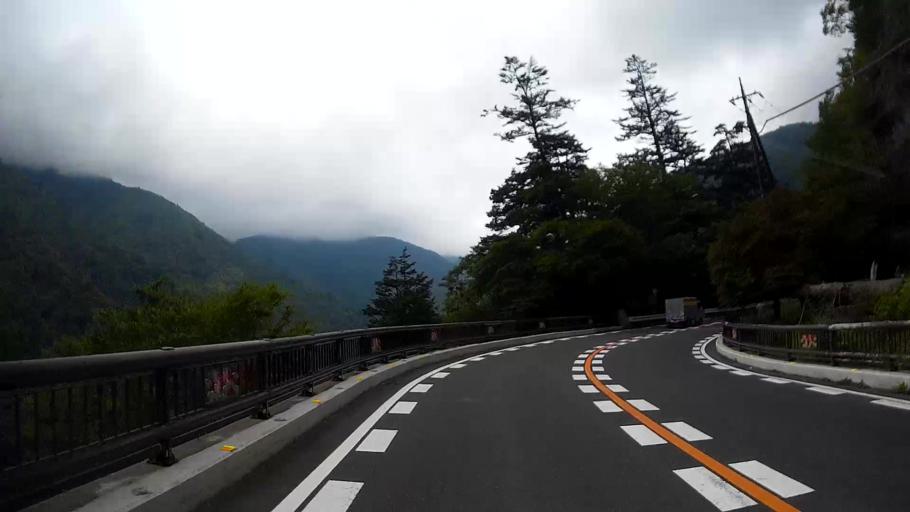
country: JP
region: Yamanashi
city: Enzan
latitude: 35.9165
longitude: 138.8308
